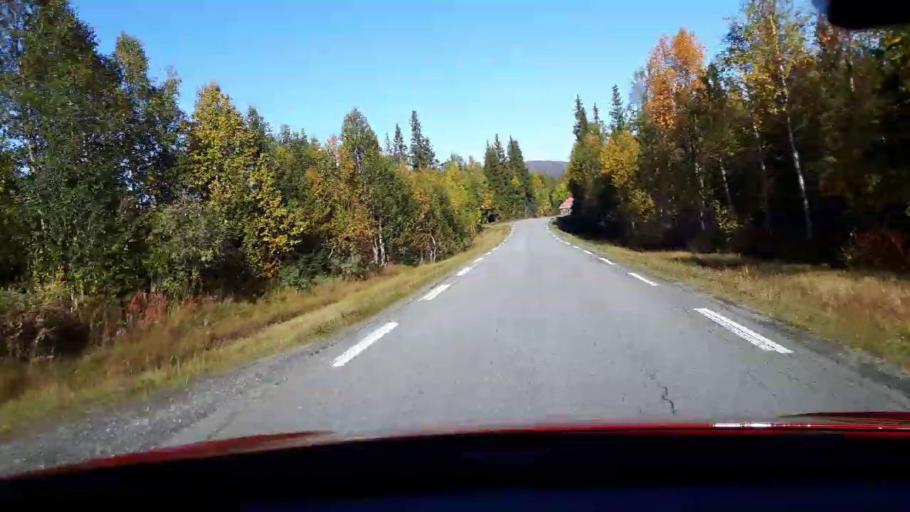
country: NO
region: Nord-Trondelag
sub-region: Lierne
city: Sandvika
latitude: 64.6249
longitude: 13.6860
